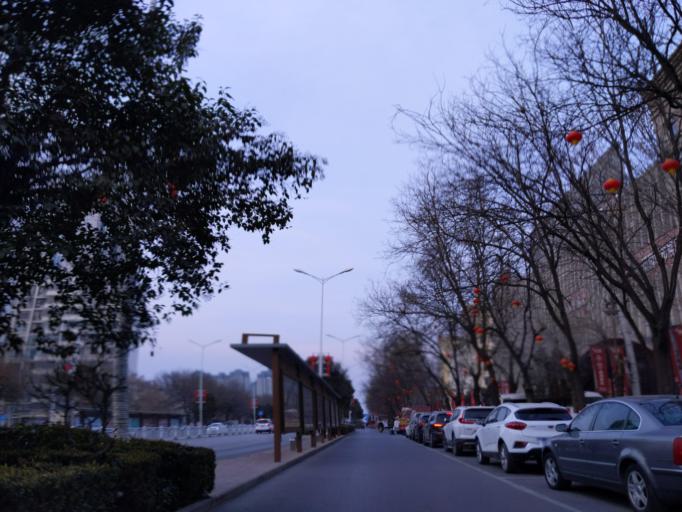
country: CN
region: Henan Sheng
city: Puyang
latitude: 35.7784
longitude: 115.0206
